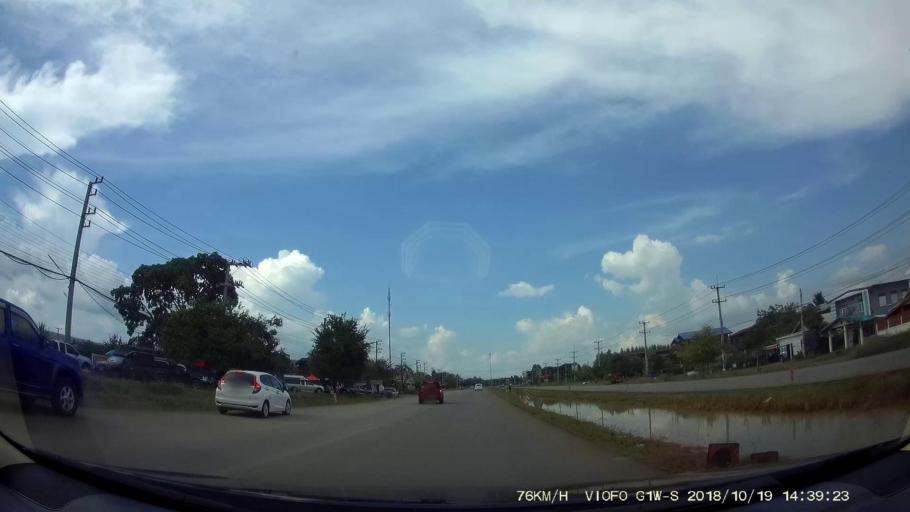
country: TH
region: Chaiyaphum
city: Kaeng Khro
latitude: 16.2252
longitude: 102.1952
